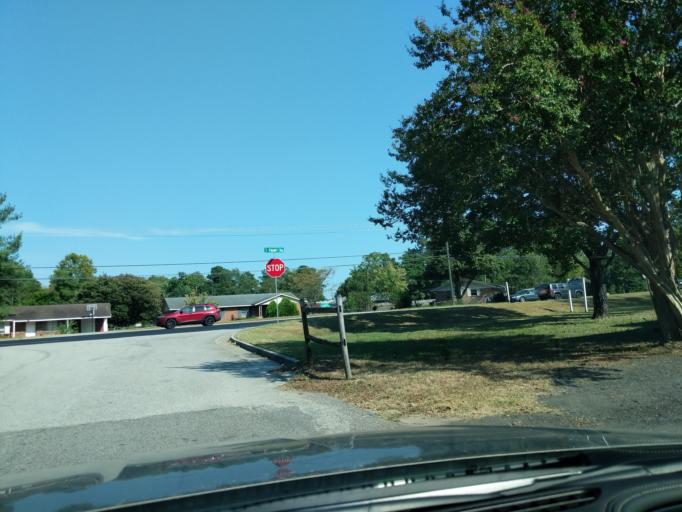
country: US
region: Georgia
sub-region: Columbia County
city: Evans
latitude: 33.5002
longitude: -82.1400
